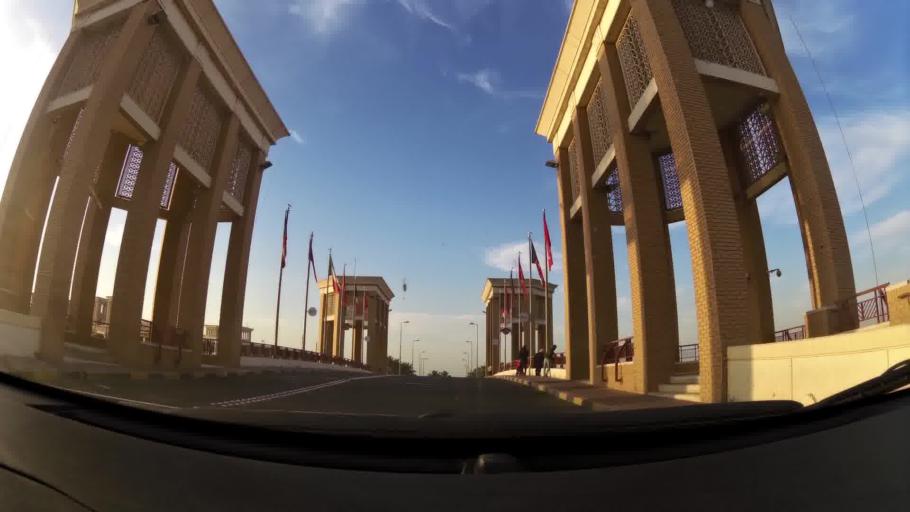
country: KW
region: Al Asimah
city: Kuwait City
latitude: 29.3898
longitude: 47.9839
